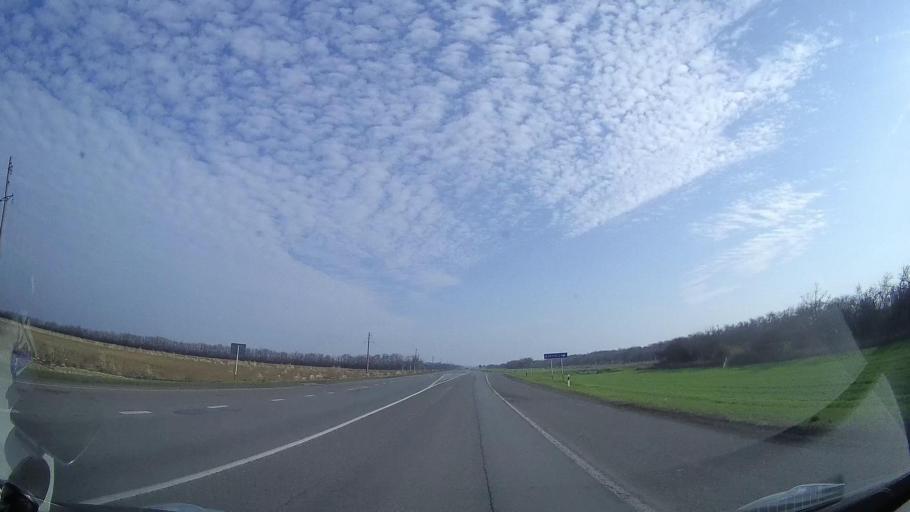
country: RU
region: Rostov
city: Gigant
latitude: 46.5239
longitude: 41.2603
